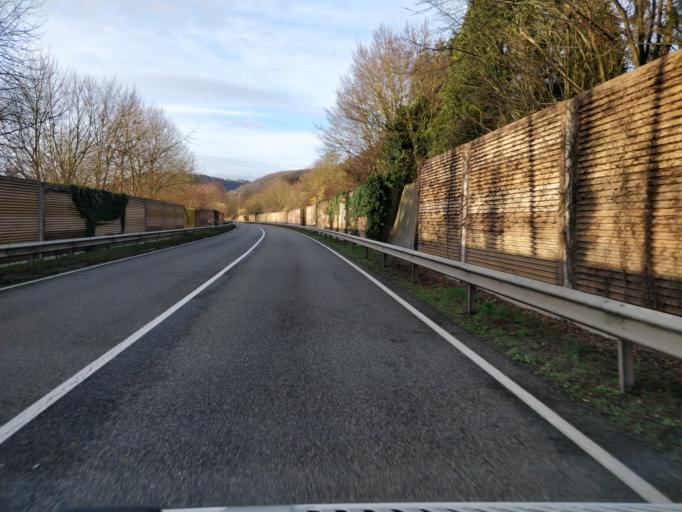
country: DE
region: Rheinland-Pfalz
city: Rheinbrohl
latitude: 50.5001
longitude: 7.3342
